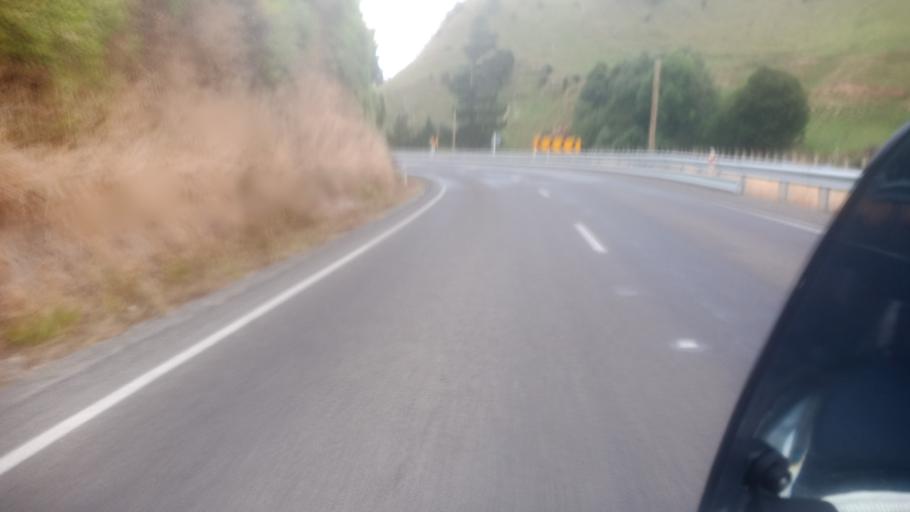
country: NZ
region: Bay of Plenty
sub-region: Opotiki District
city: Opotiki
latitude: -38.3781
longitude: 177.4692
